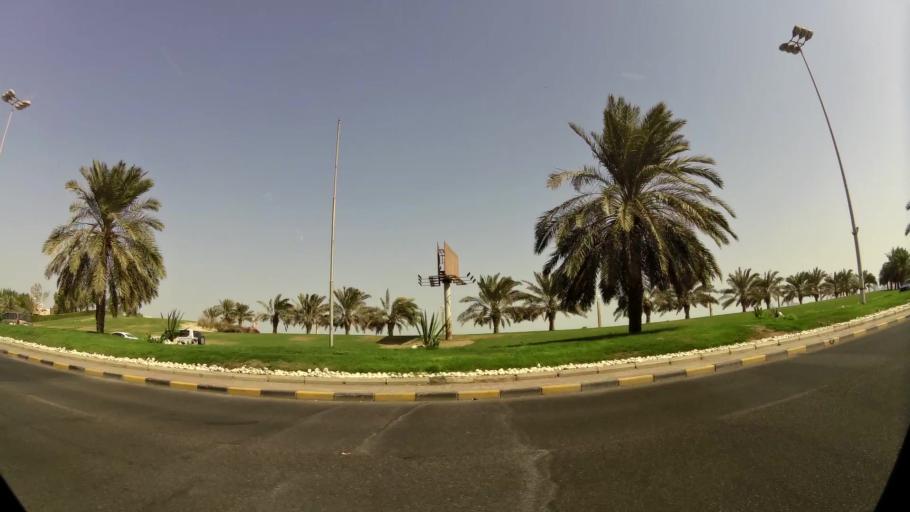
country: KW
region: Al Asimah
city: Ad Dasmah
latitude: 29.3588
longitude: 48.0254
